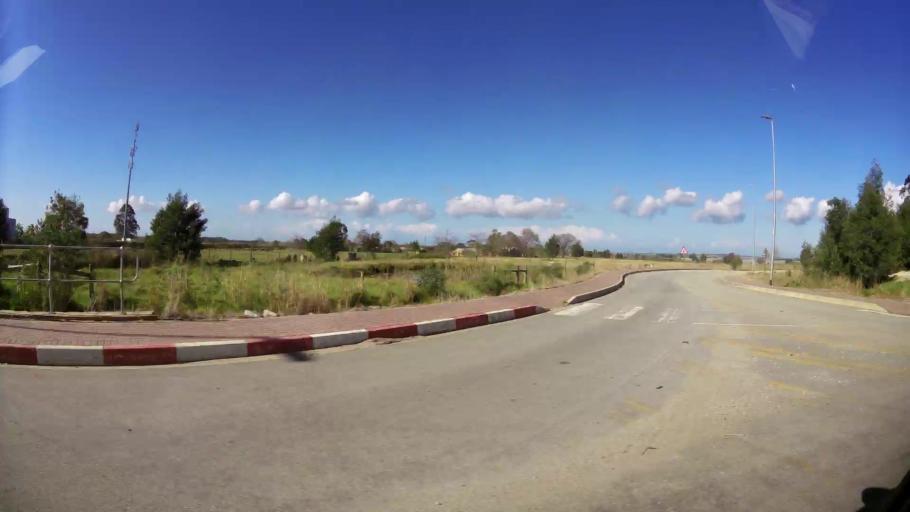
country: ZA
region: Western Cape
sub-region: Eden District Municipality
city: George
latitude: -33.9553
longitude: 22.3961
